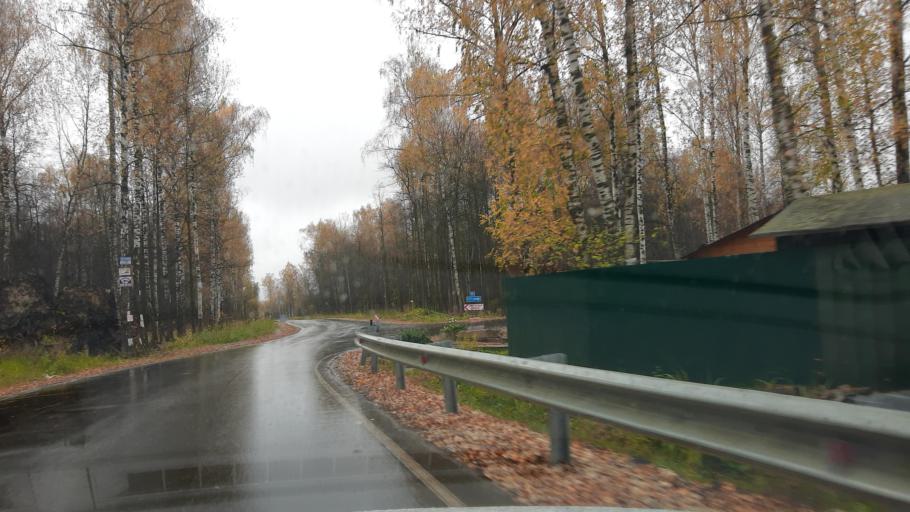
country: RU
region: Moskovskaya
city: Imeni Vorovskogo
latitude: 55.7868
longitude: 38.3633
